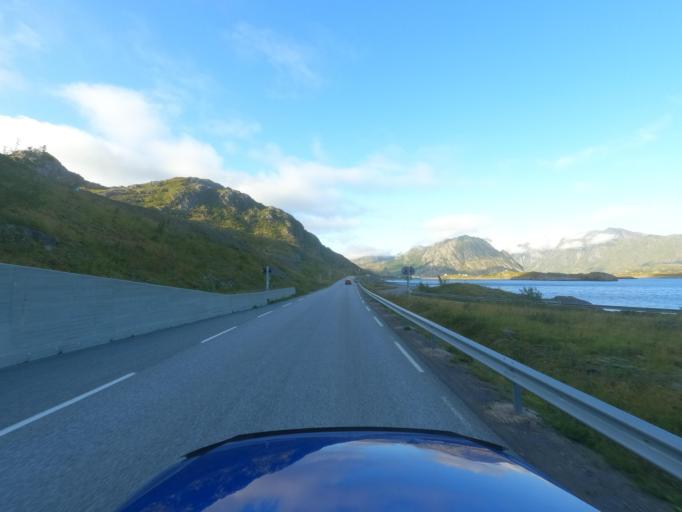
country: NO
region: Nordland
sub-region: Moskenes
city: Reine
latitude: 67.9915
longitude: 13.1662
